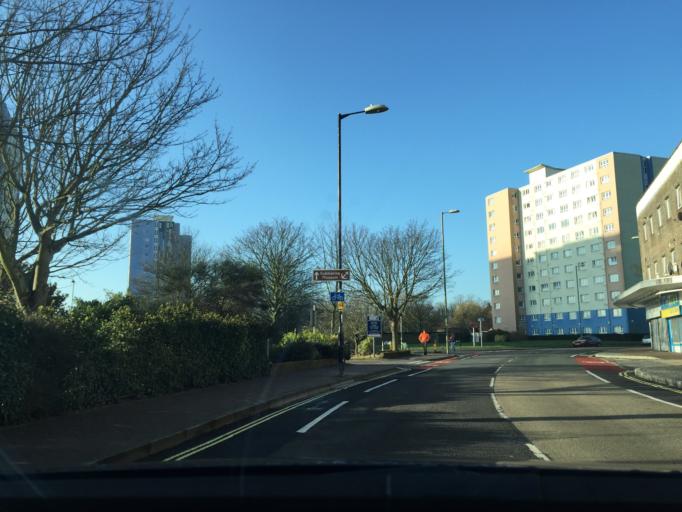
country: GB
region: England
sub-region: Hampshire
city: Gosport
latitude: 50.7946
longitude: -1.1182
